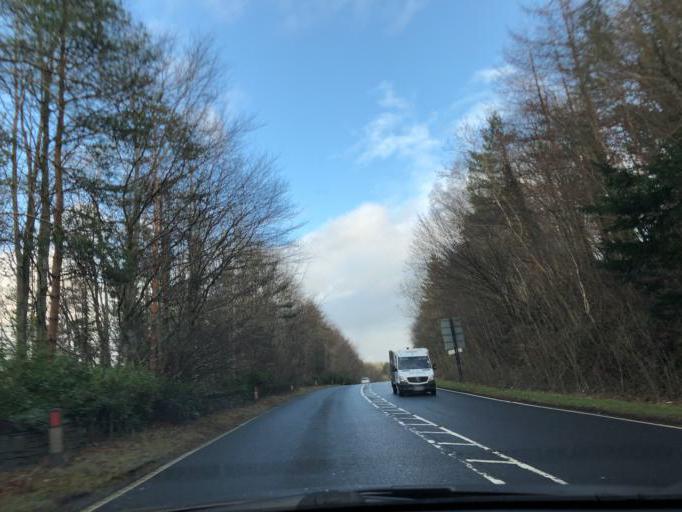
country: GB
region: England
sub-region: Cumbria
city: Grange-over-Sands
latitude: 54.2628
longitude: -2.9866
